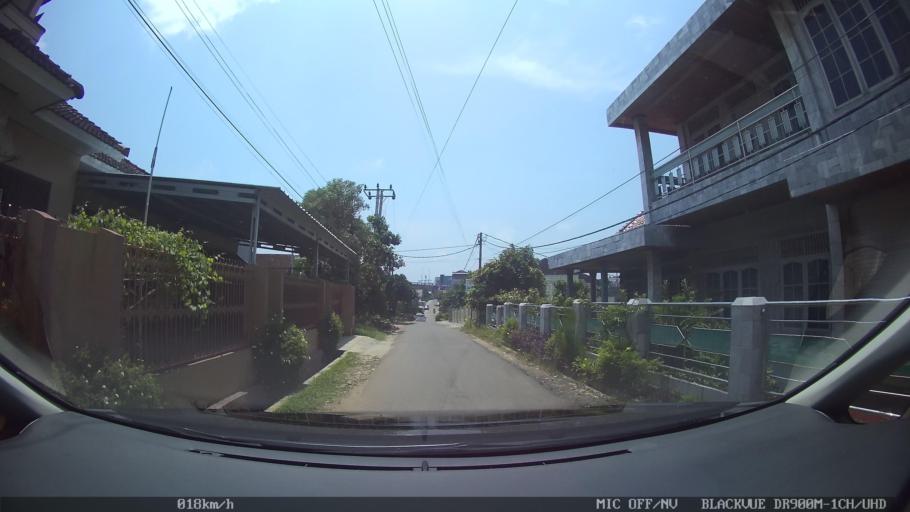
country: ID
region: Lampung
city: Kedaton
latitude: -5.3719
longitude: 105.2718
